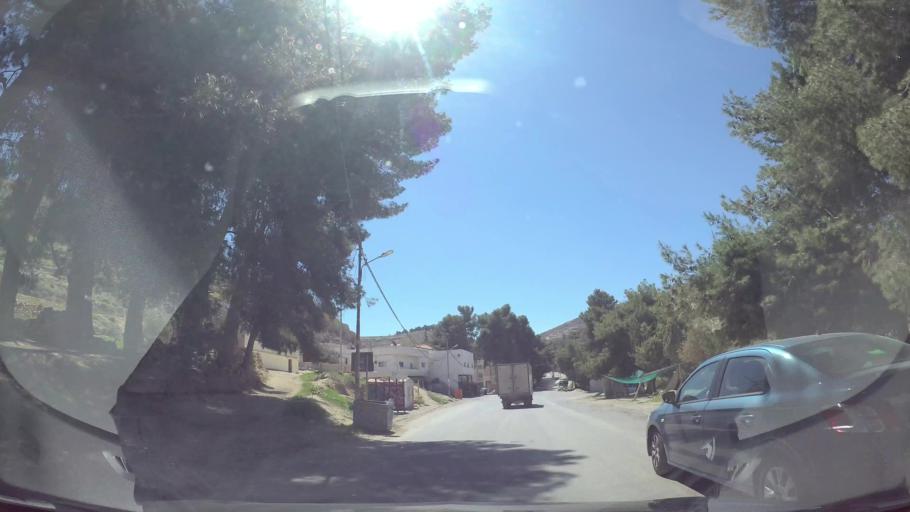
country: JO
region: Tafielah
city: At Tafilah
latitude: 30.8186
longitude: 35.5867
